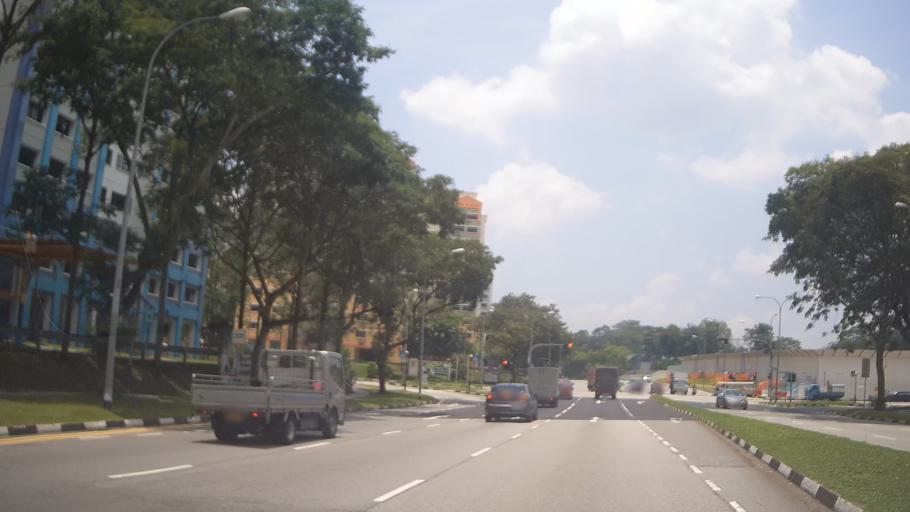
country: MY
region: Johor
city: Johor Bahru
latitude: 1.4463
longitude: 103.7933
